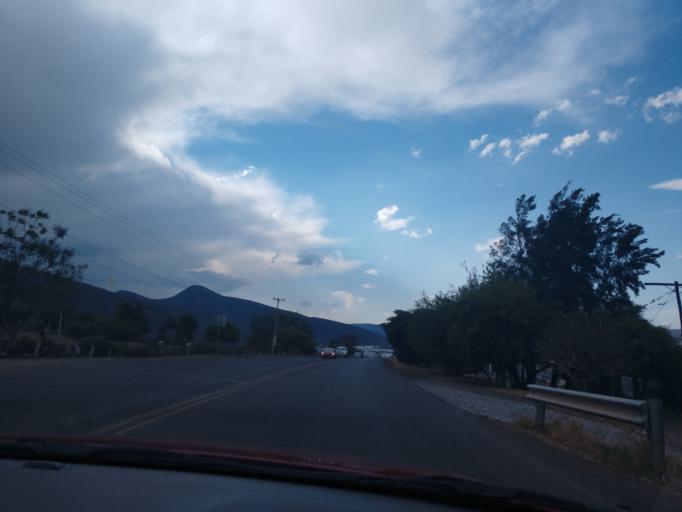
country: MX
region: Jalisco
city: Jocotepec
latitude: 20.2266
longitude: -103.4153
